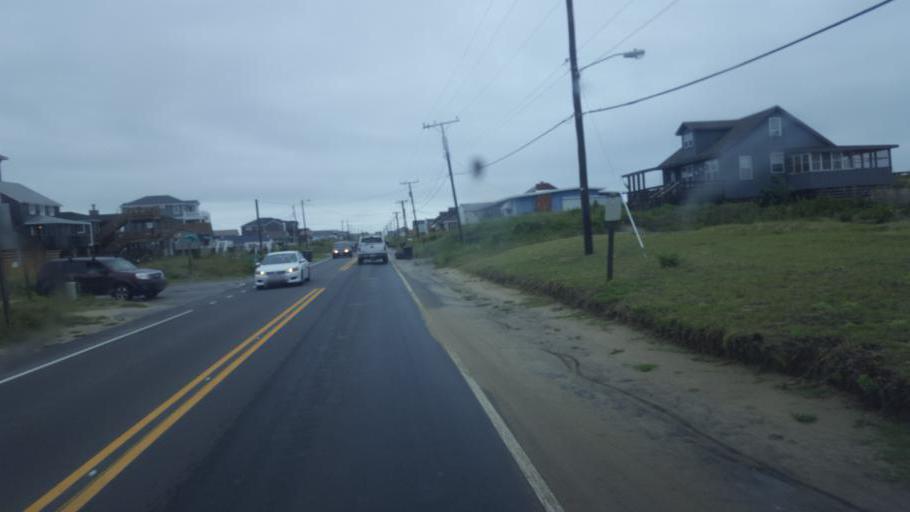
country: US
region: North Carolina
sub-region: Dare County
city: Kill Devil Hills
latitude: 36.0440
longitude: -75.6754
